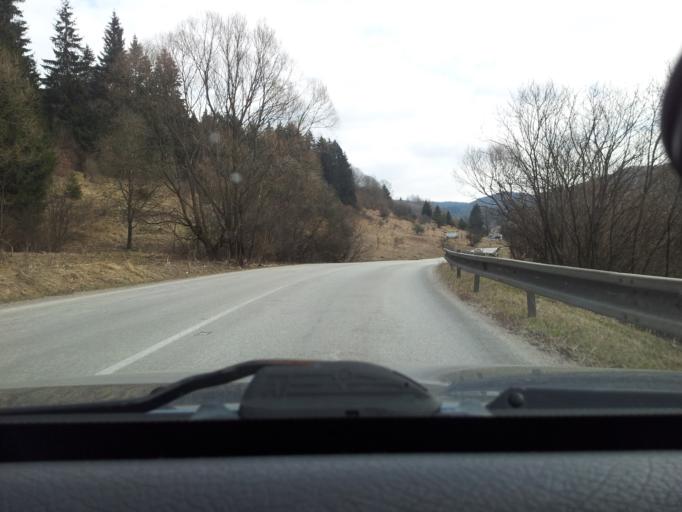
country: SK
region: Banskobystricky
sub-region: Okres Ziar nad Hronom
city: Kremnica
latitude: 48.7707
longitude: 18.9017
